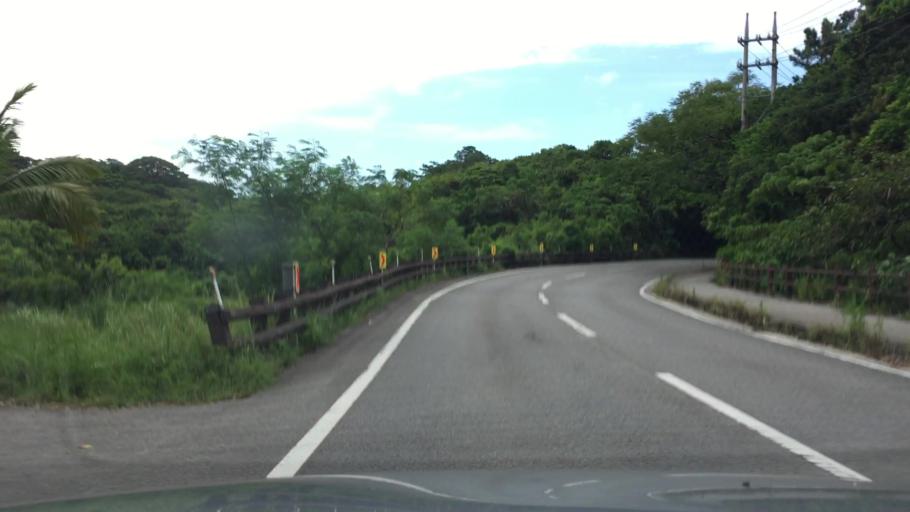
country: JP
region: Okinawa
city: Ishigaki
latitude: 24.4558
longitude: 124.1379
